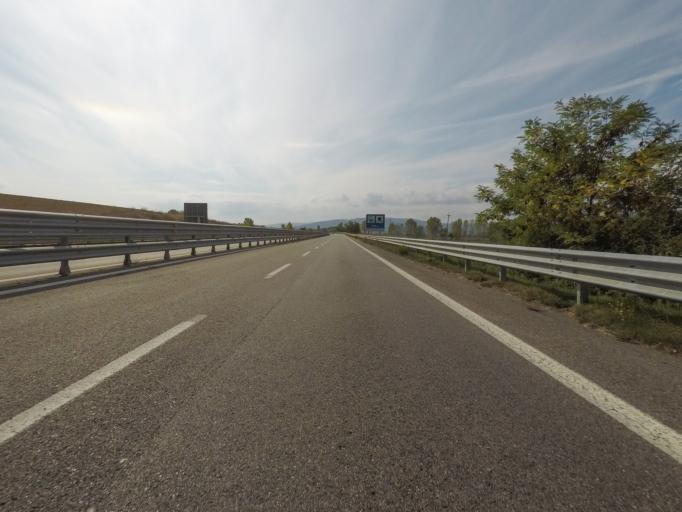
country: IT
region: Tuscany
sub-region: Provincia di Siena
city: Rosia
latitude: 43.2332
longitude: 11.2771
